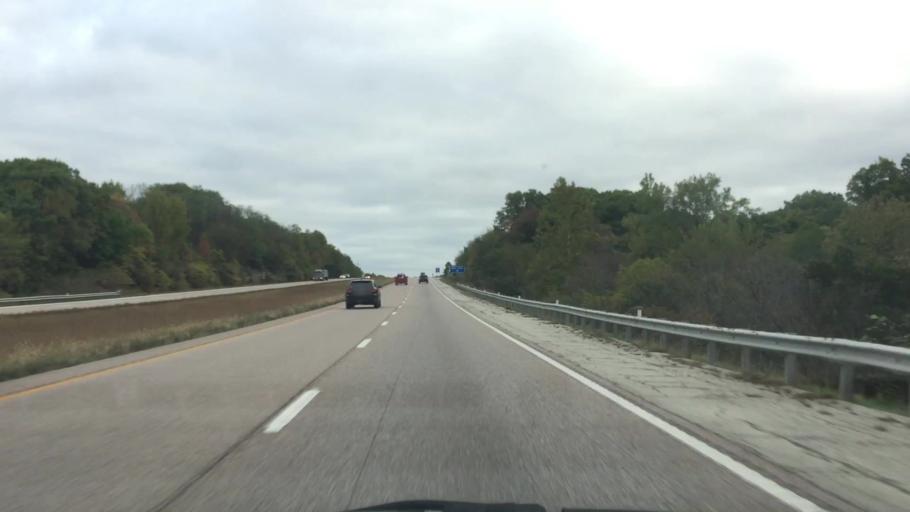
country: US
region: Missouri
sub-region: Clinton County
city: Lathrop
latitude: 39.4702
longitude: -94.3141
